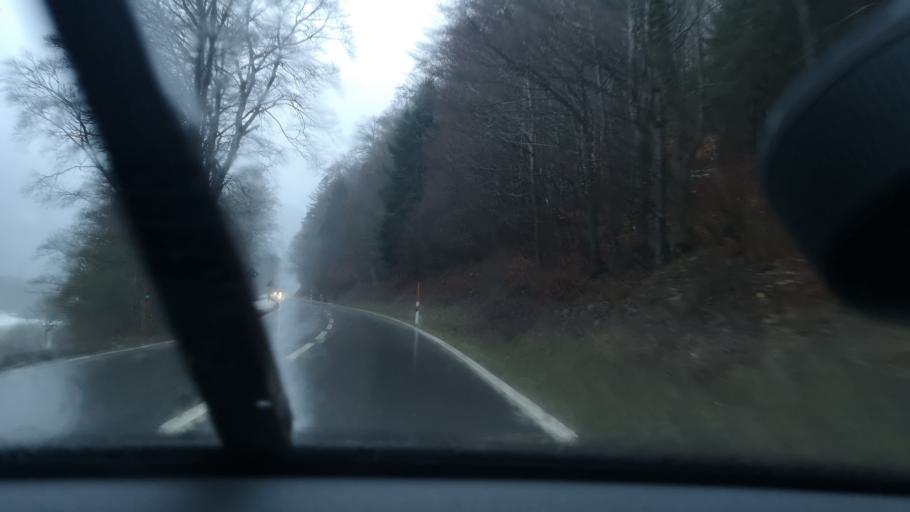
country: CH
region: Neuchatel
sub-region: Le Locle District
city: Les Ponts-de-Martel
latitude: 46.9603
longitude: 6.7638
